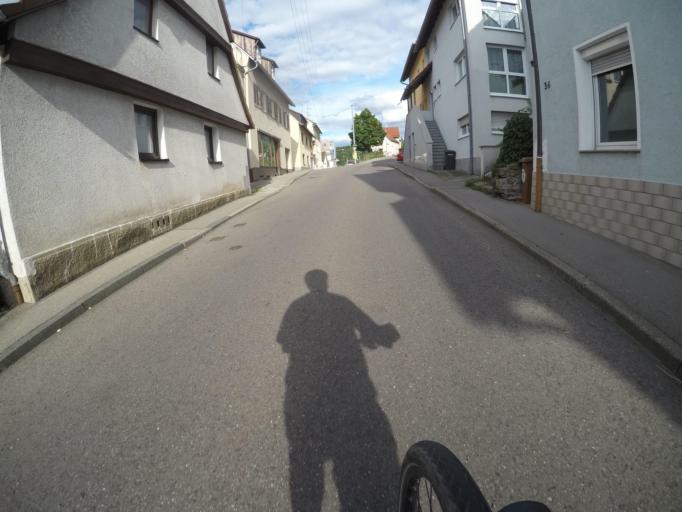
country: DE
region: Baden-Wuerttemberg
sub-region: Regierungsbezirk Stuttgart
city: Stuttgart Feuerbach
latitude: 48.7777
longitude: 9.1262
